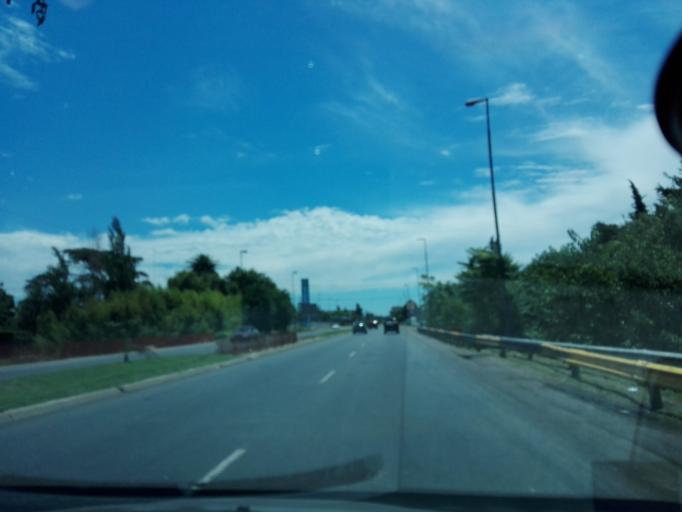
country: AR
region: Buenos Aires
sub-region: Partido de La Plata
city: La Plata
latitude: -34.8919
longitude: -57.9942
